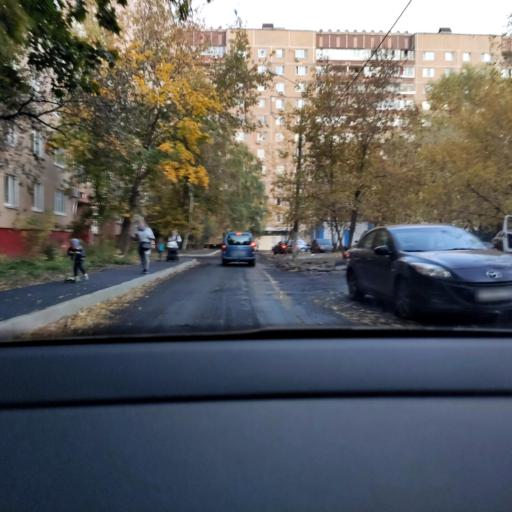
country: RU
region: Moscow
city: Otradnoye
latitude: 55.8663
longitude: 37.5925
